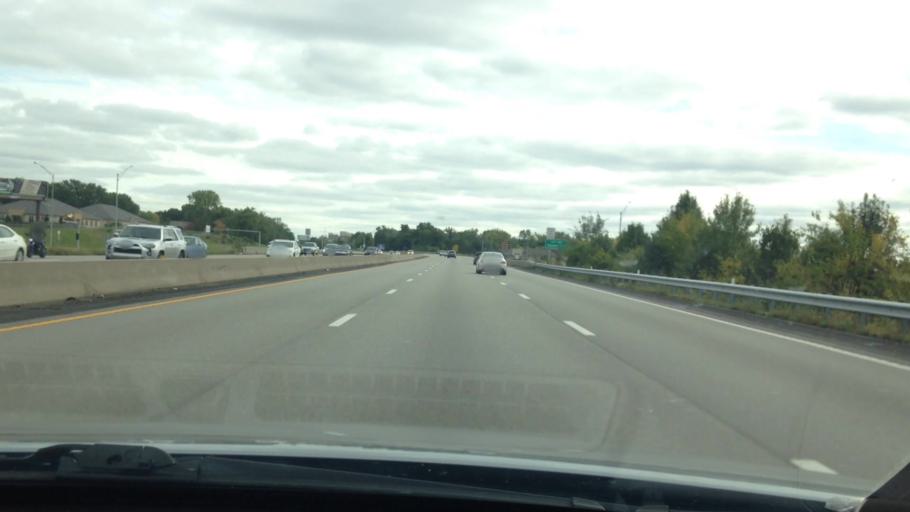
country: US
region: Missouri
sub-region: Platte County
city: Parkville
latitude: 39.2263
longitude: -94.6512
